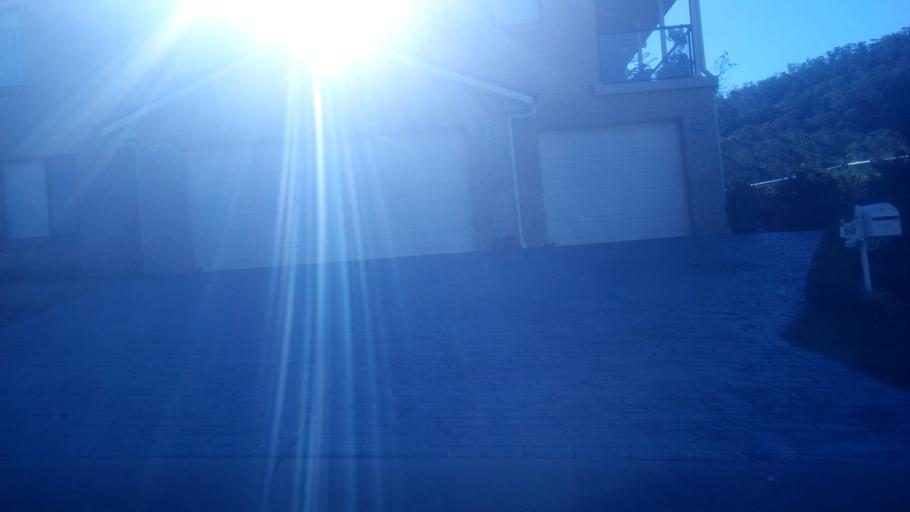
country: AU
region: New South Wales
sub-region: Wollongong
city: Mount Keira
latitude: -34.4149
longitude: 150.8458
